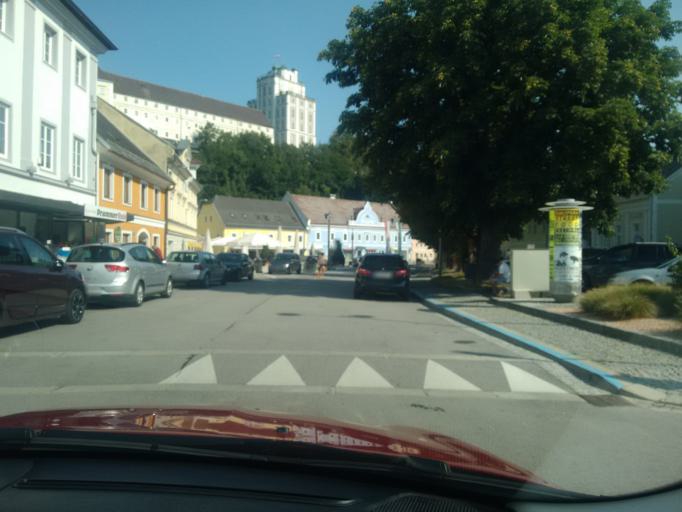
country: AT
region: Upper Austria
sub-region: Politischer Bezirk Kirchdorf an der Krems
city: Kremsmunster
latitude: 48.0531
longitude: 14.1316
